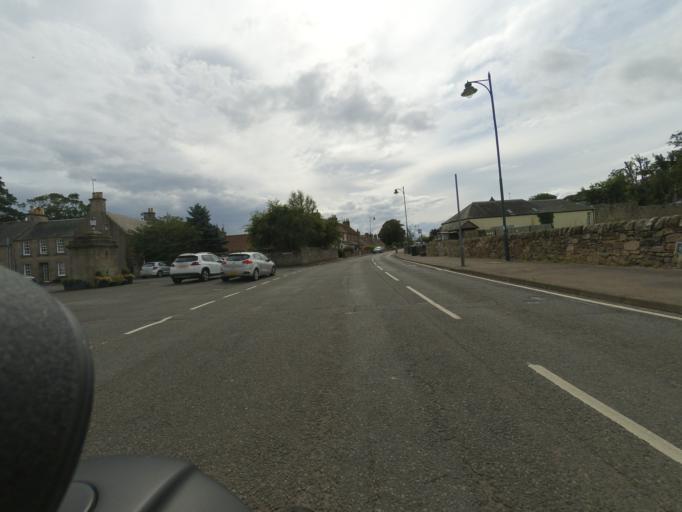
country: GB
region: Scotland
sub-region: Fife
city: Anstruther
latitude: 56.2991
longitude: -2.6596
